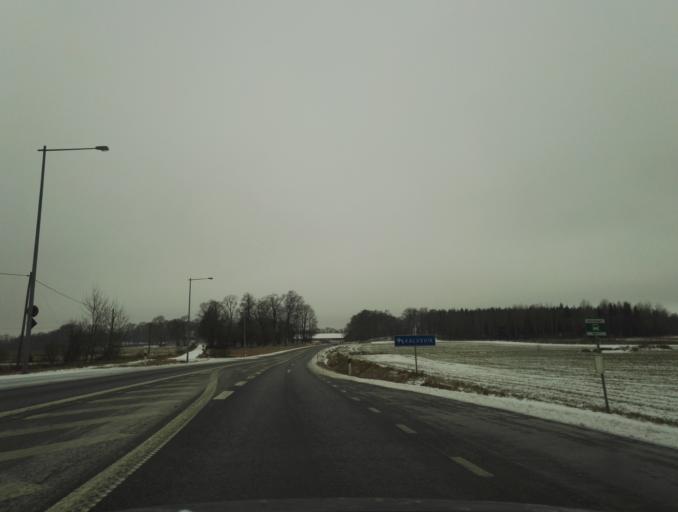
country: SE
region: Kronoberg
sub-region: Vaxjo Kommun
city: Gemla
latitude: 56.7827
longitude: 14.6028
